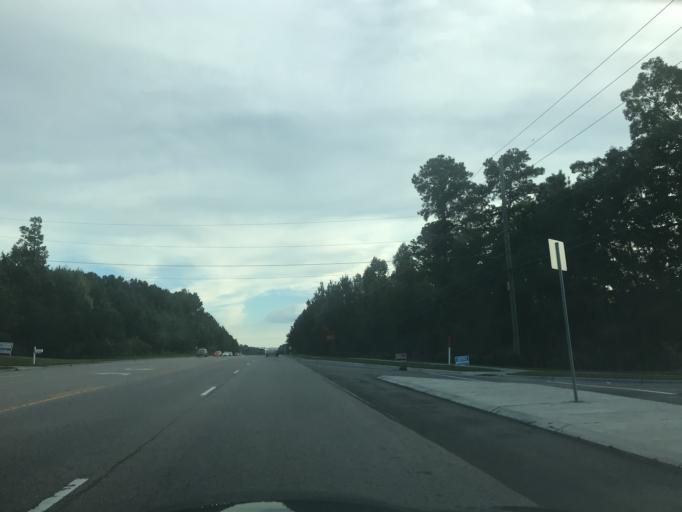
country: US
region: North Carolina
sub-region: Wake County
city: Green Level
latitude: 35.7766
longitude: -78.8728
